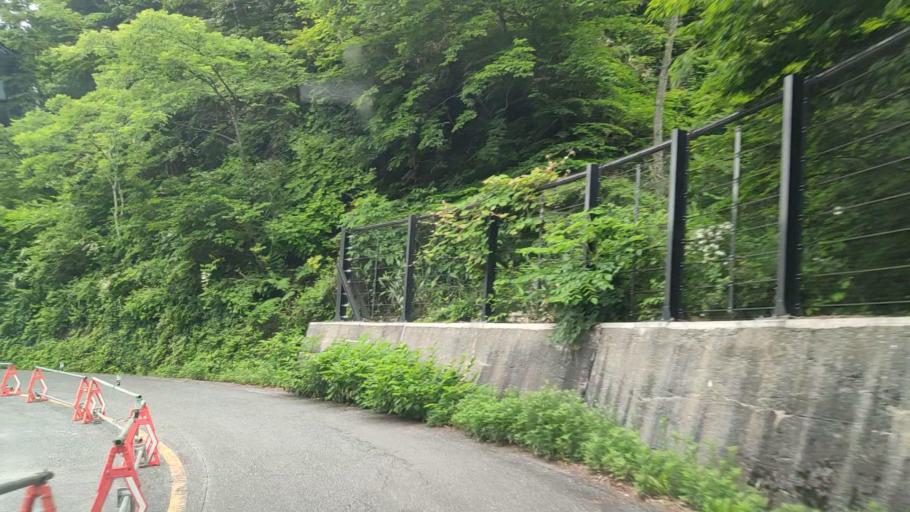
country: JP
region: Tottori
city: Yonago
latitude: 35.3486
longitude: 133.5496
